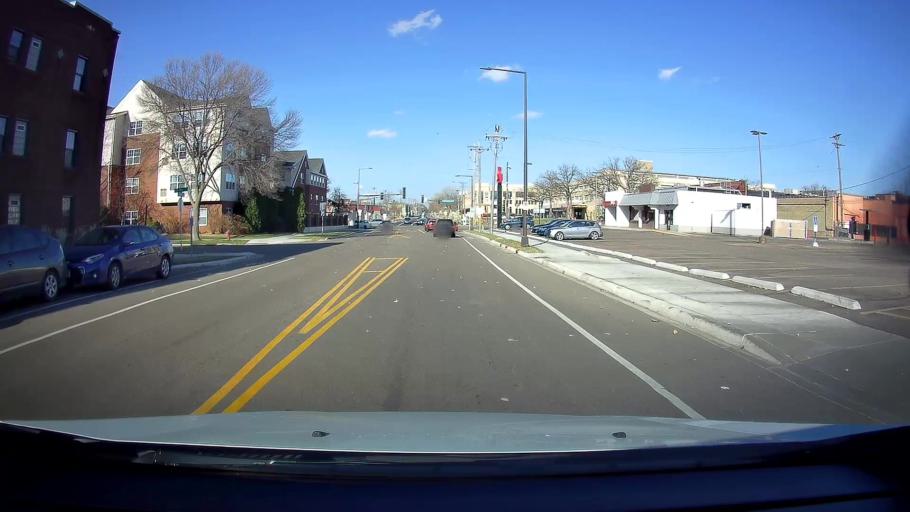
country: US
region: Minnesota
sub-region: Ramsey County
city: Falcon Heights
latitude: 44.9548
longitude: -93.1772
